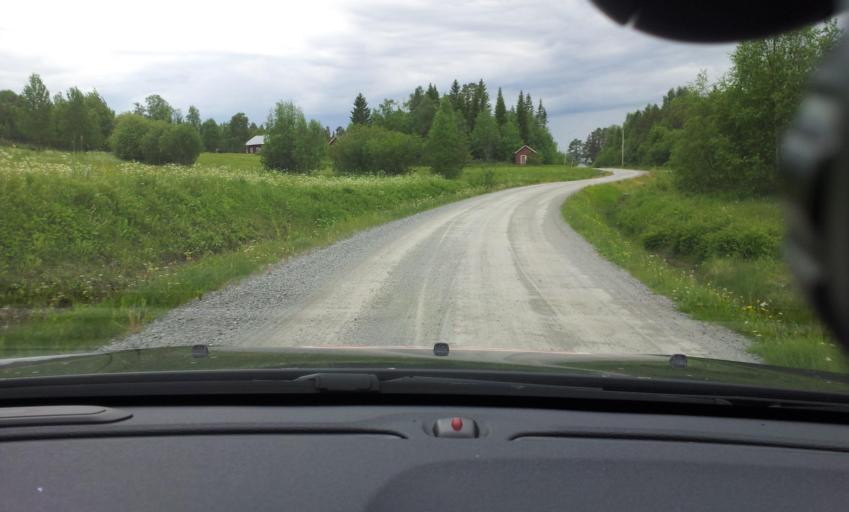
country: SE
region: Jaemtland
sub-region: OEstersunds Kommun
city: Brunflo
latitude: 62.9787
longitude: 14.6932
